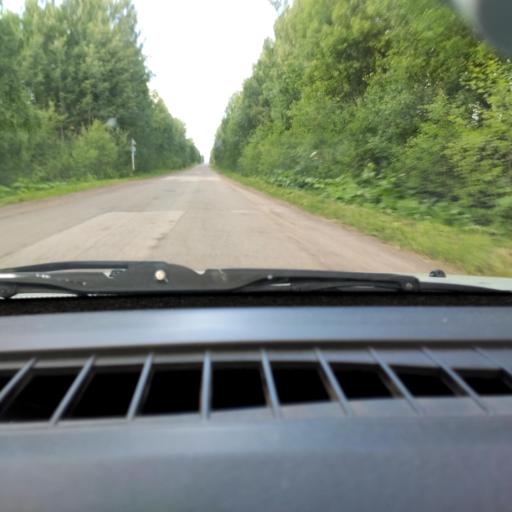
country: RU
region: Perm
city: Kukushtan
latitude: 57.2760
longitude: 56.5351
